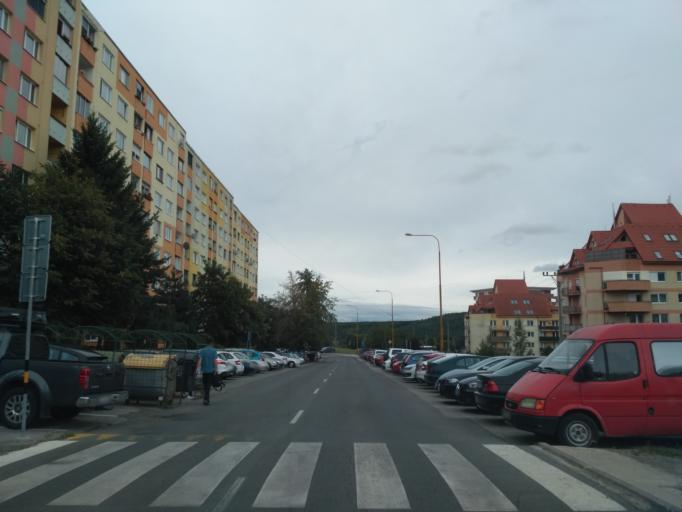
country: SK
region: Kosicky
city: Kosice
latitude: 48.7144
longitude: 21.2067
